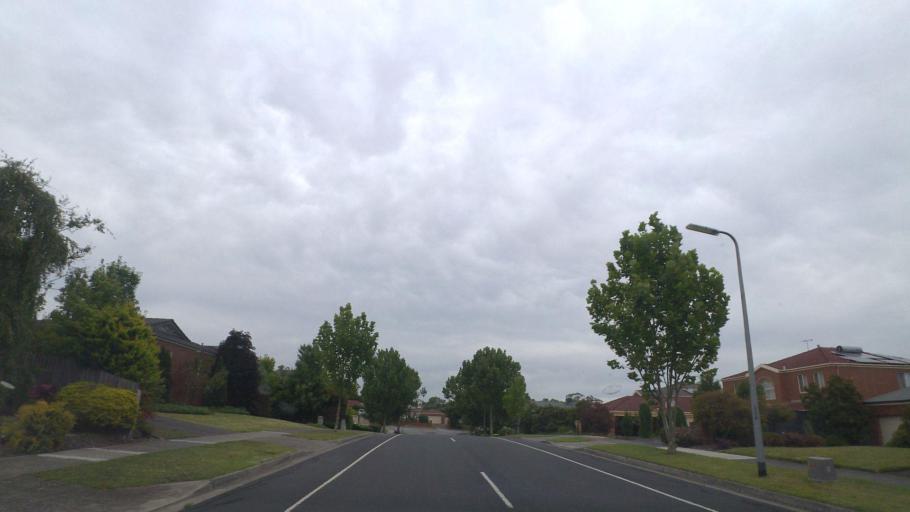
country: AU
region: Victoria
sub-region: Yarra Ranges
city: Kilsyth
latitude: -37.7807
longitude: 145.3358
